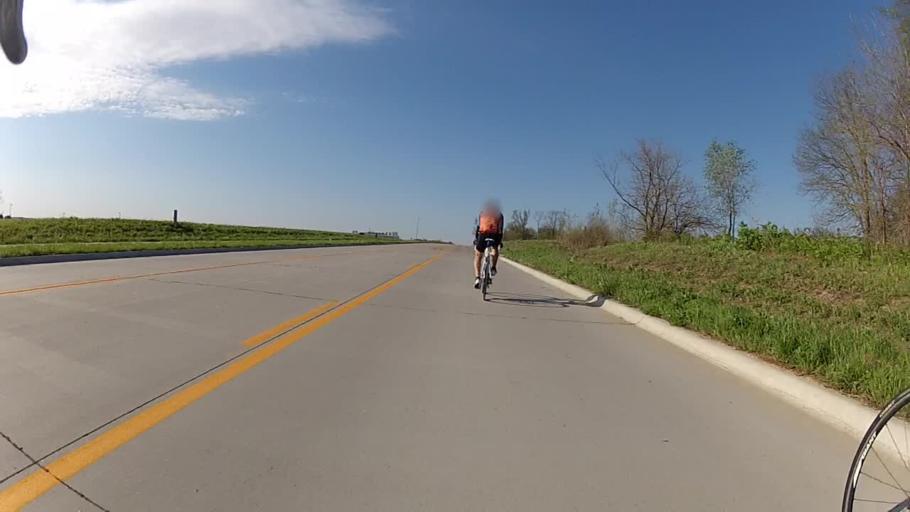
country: US
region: Kansas
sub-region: Riley County
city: Ogden
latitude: 39.1441
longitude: -96.6820
